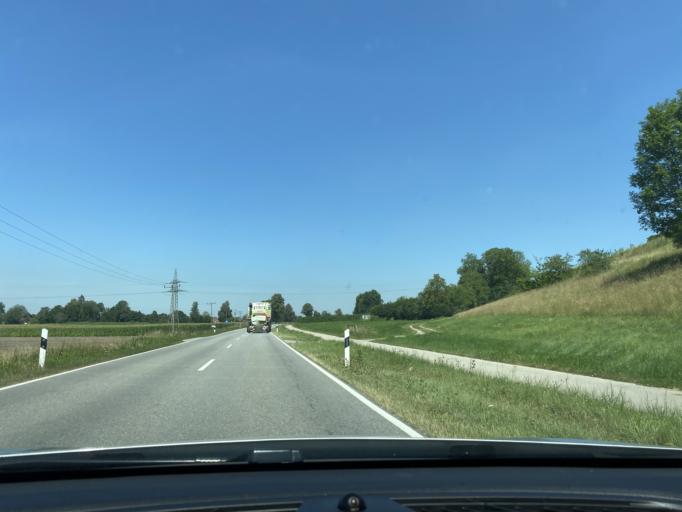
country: DE
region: Bavaria
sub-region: Upper Bavaria
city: Moosinning
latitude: 48.2644
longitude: 11.8458
